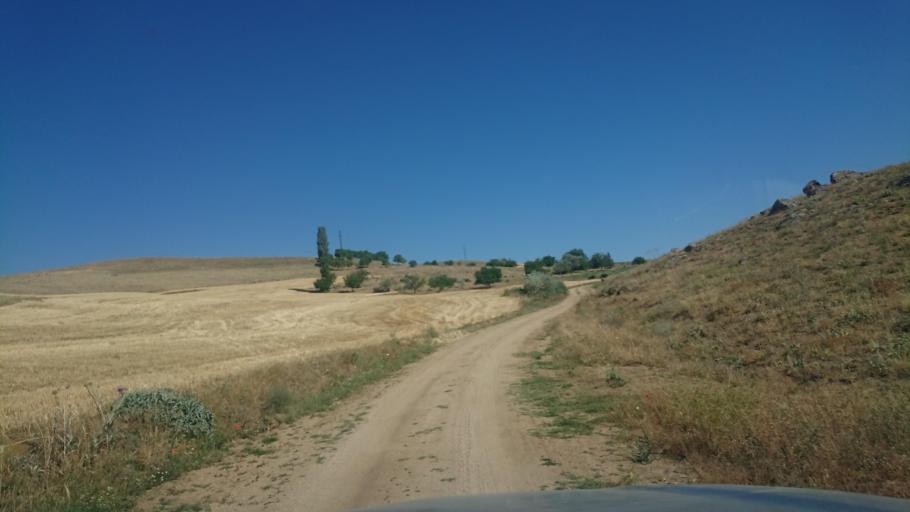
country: TR
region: Aksaray
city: Agacoren
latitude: 38.9046
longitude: 33.8997
